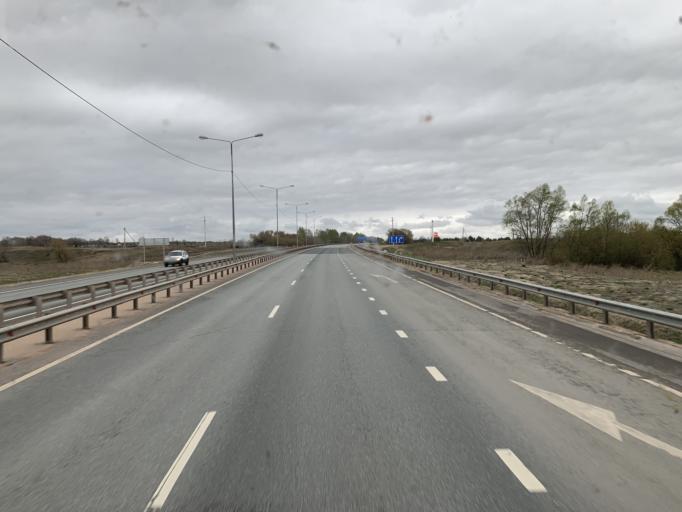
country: RU
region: Ulyanovsk
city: Kanadey
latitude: 53.1502
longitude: 47.5876
